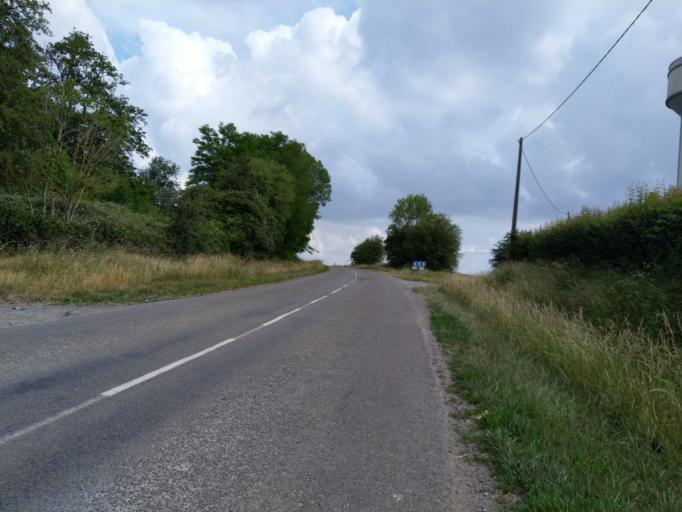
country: FR
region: Nord-Pas-de-Calais
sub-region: Departement du Nord
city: Boussois
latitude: 50.3260
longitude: 4.0082
